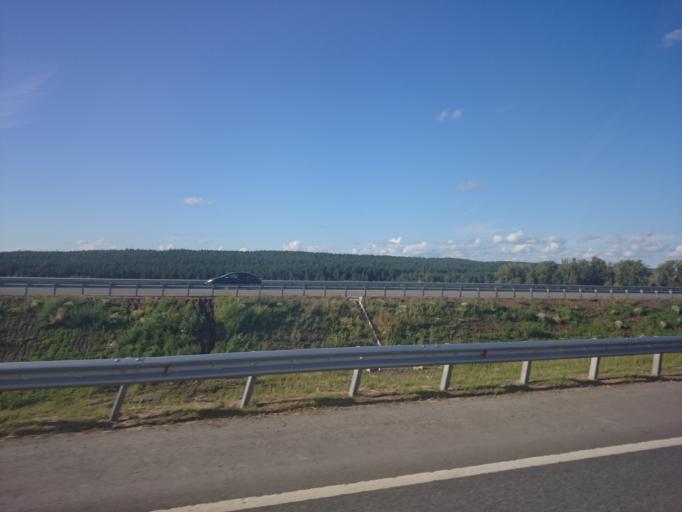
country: RU
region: Tatarstan
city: Mamadysh
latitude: 55.7125
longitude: 51.5956
